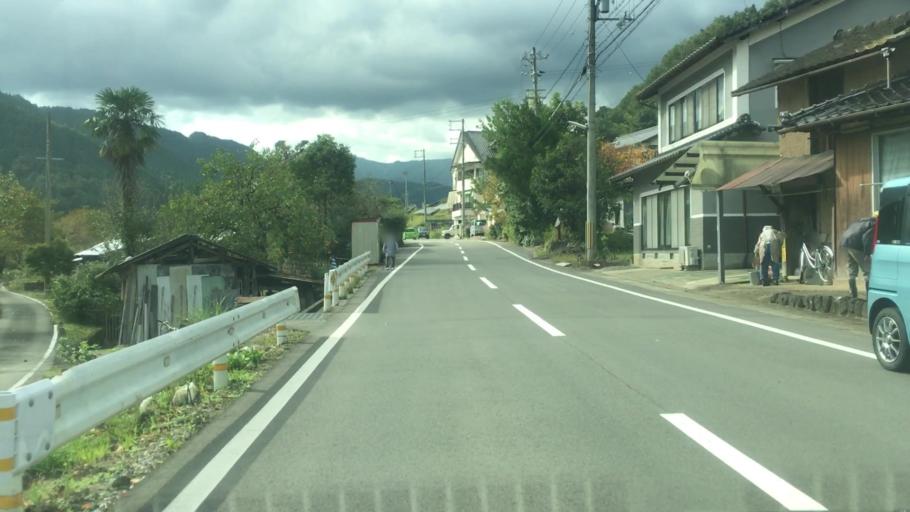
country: JP
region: Hyogo
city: Toyooka
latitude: 35.4092
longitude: 134.7527
